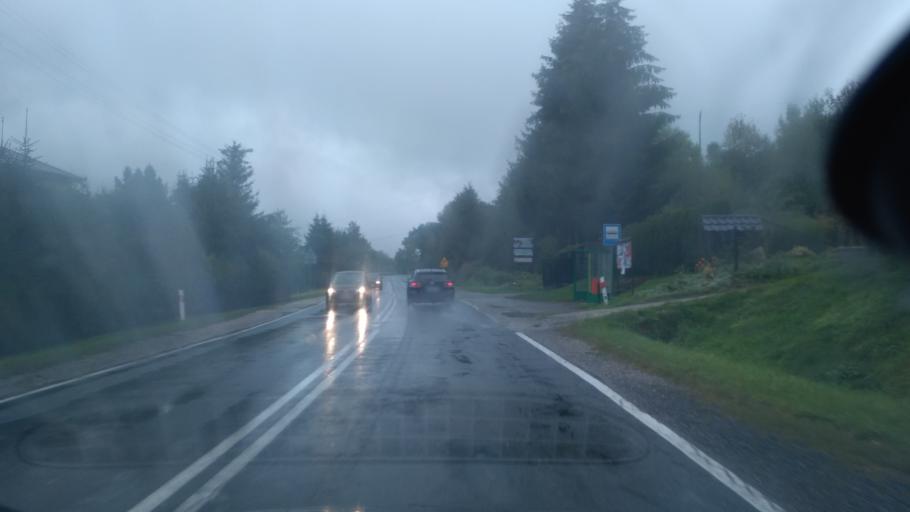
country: PL
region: Subcarpathian Voivodeship
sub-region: Powiat ropczycko-sedziszowski
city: Niedzwiada
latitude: 50.0099
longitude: 21.5536
